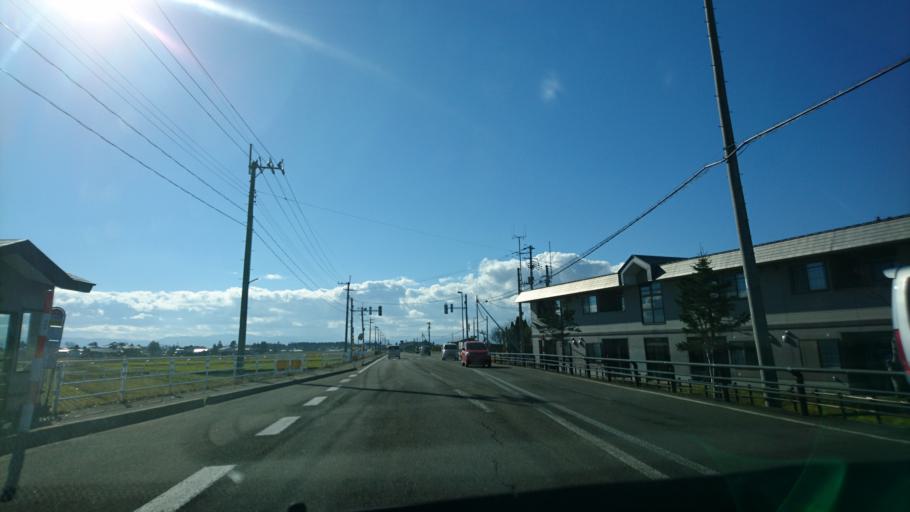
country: JP
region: Akita
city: Yokotemachi
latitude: 39.2837
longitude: 140.5159
